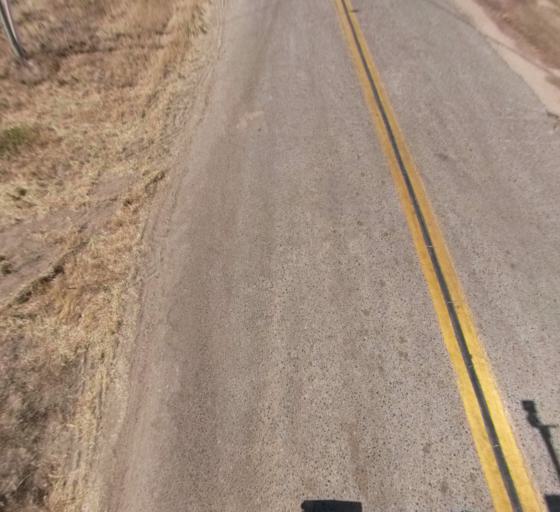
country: US
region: California
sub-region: Madera County
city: Parkwood
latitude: 36.8657
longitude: -120.0284
